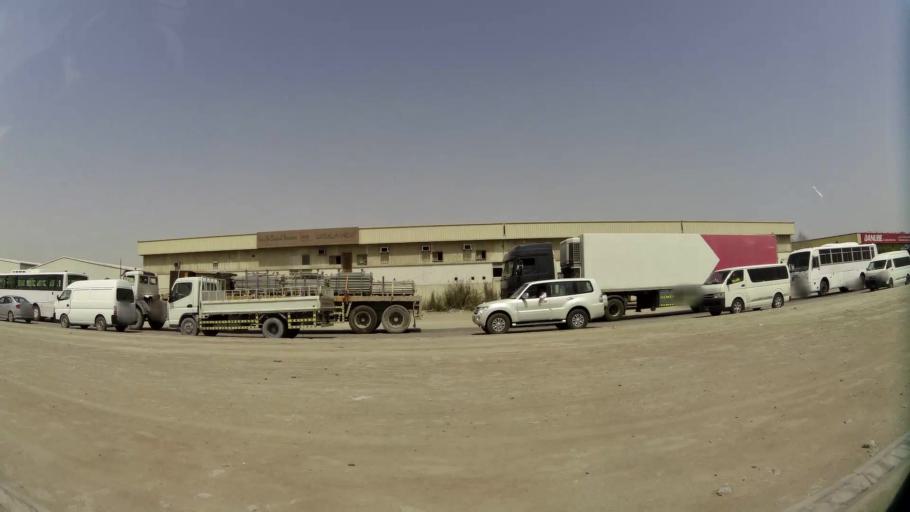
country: QA
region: Baladiyat ar Rayyan
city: Ar Rayyan
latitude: 25.1844
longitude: 51.4313
